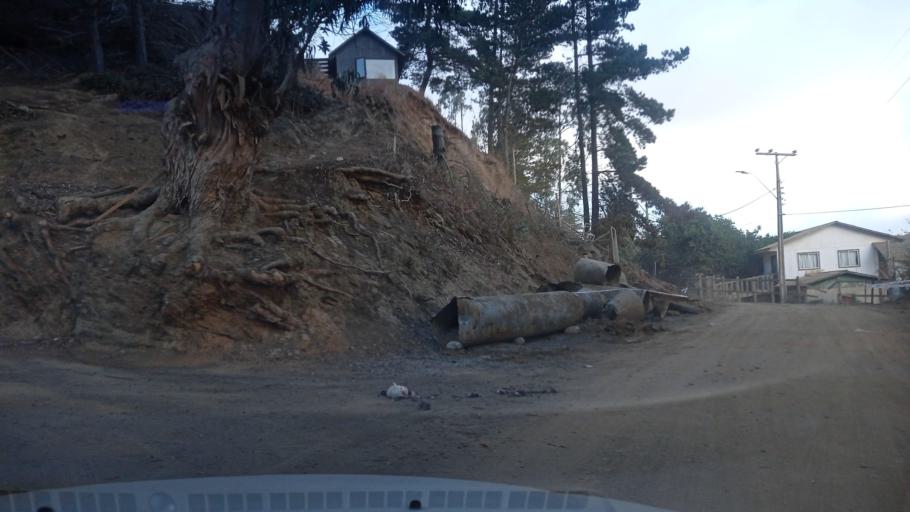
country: CL
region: O'Higgins
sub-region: Provincia de Colchagua
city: Santa Cruz
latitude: -34.4820
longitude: -72.0104
